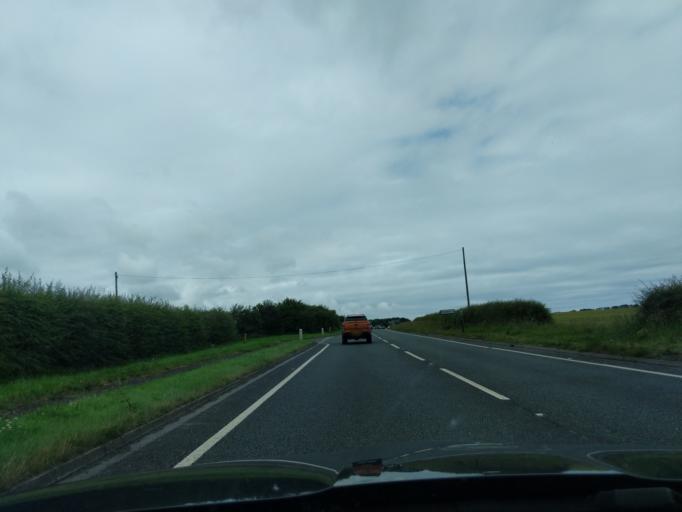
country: GB
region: England
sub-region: Northumberland
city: Ancroft
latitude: 55.7153
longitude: -1.9781
